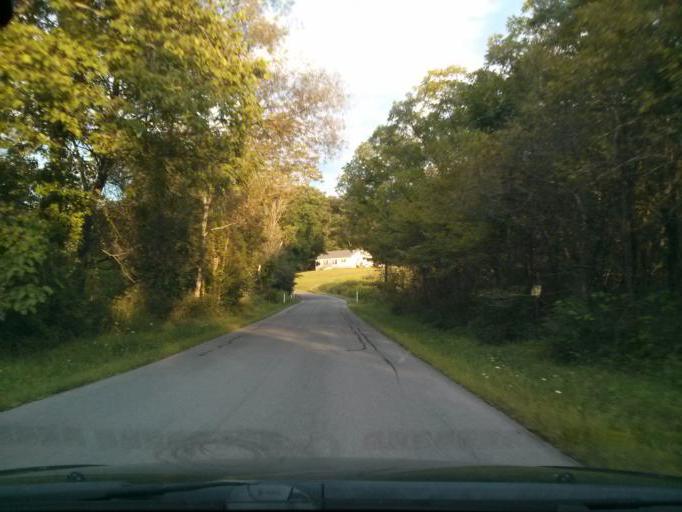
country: US
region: Pennsylvania
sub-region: Centre County
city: Park Forest Village
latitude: 40.8337
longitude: -77.9282
